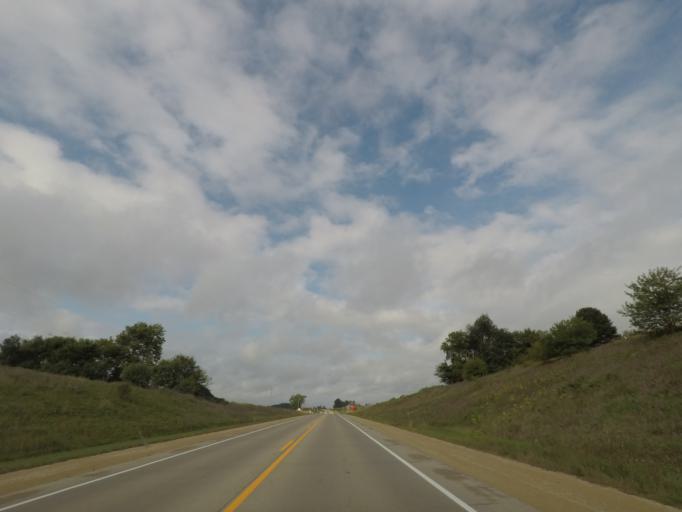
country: US
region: Wisconsin
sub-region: Dane County
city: Deerfield
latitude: 43.0368
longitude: -89.1013
